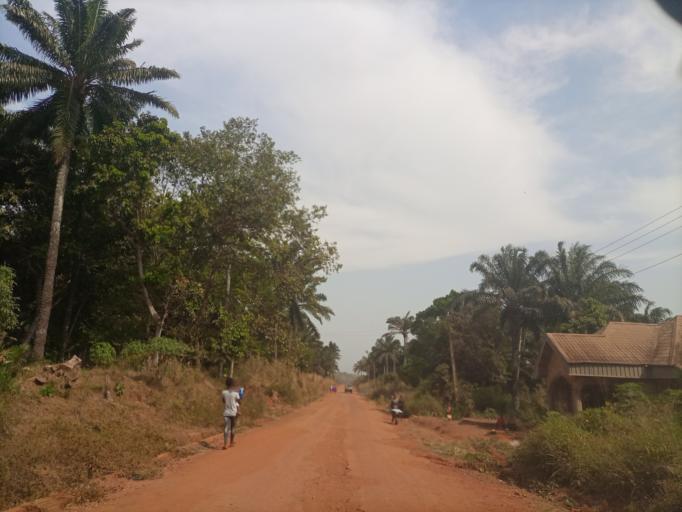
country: NG
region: Enugu
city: Opi
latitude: 6.8224
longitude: 7.4738
